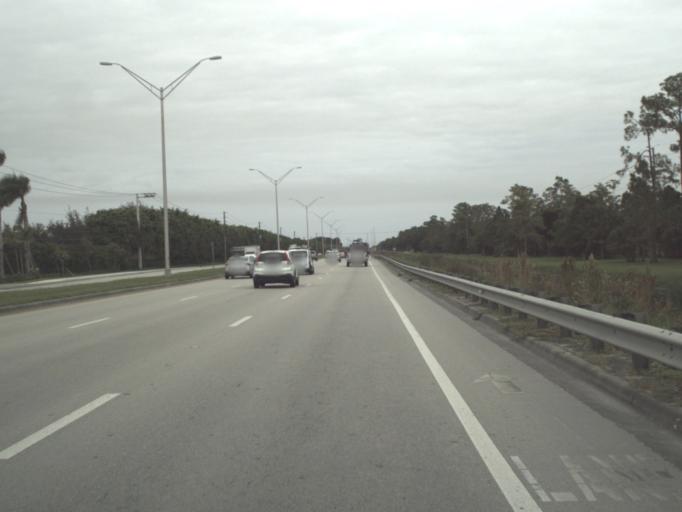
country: US
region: Florida
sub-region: Collier County
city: Lely Resort
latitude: 26.0893
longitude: -81.6872
